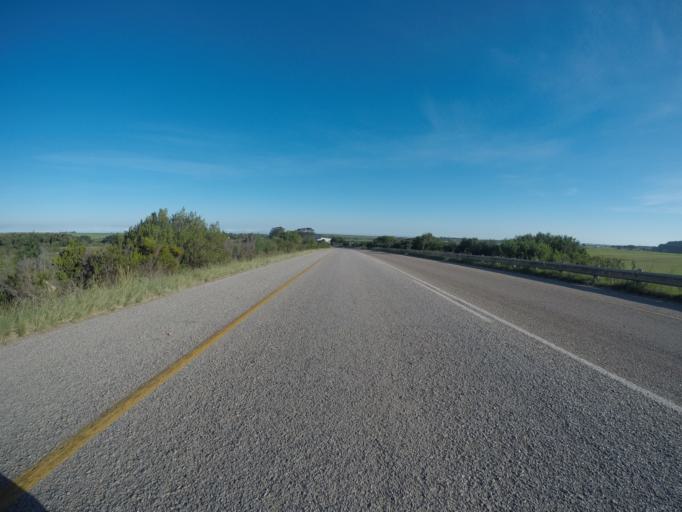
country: ZA
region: Eastern Cape
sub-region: Cacadu District Municipality
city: Kareedouw
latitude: -34.0001
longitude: 24.2352
